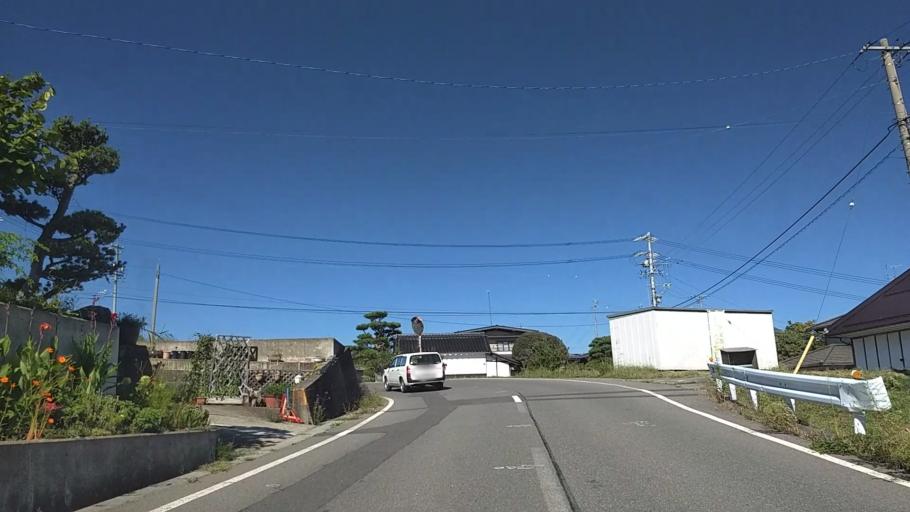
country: JP
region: Nagano
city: Nagano-shi
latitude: 36.5771
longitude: 138.1152
